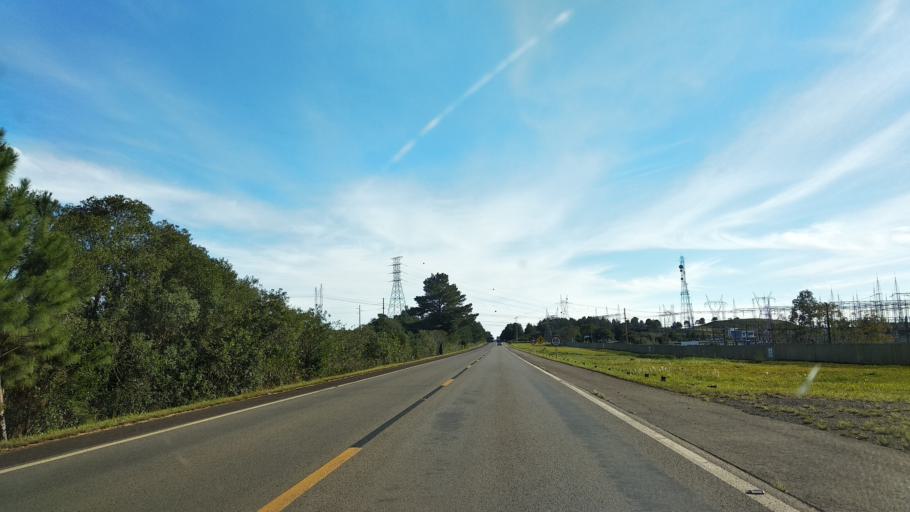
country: BR
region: Santa Catarina
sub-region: Celso Ramos
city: Celso Ramos
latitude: -27.5397
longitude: -51.4117
